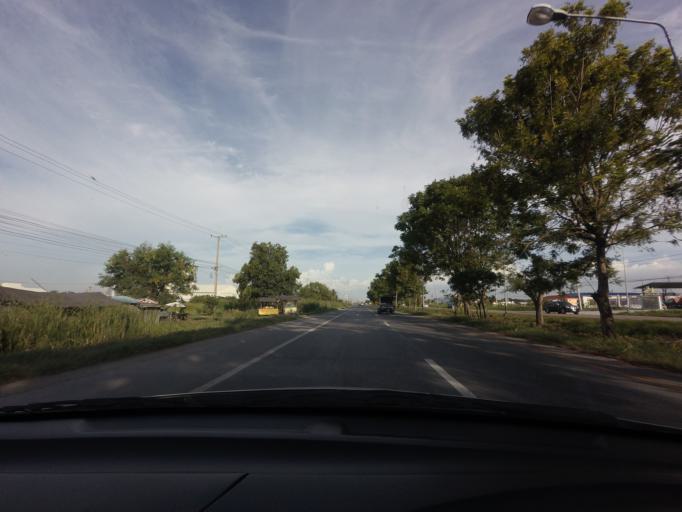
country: TH
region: Pathum Thani
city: Lat Lum Kaeo
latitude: 14.0421
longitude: 100.3432
